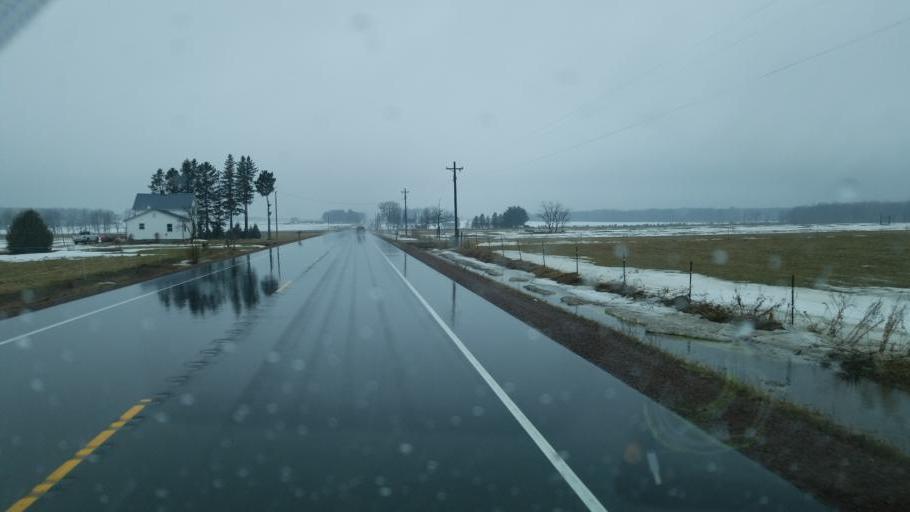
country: US
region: Wisconsin
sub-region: Marathon County
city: Spencer
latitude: 44.6561
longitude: -90.3113
